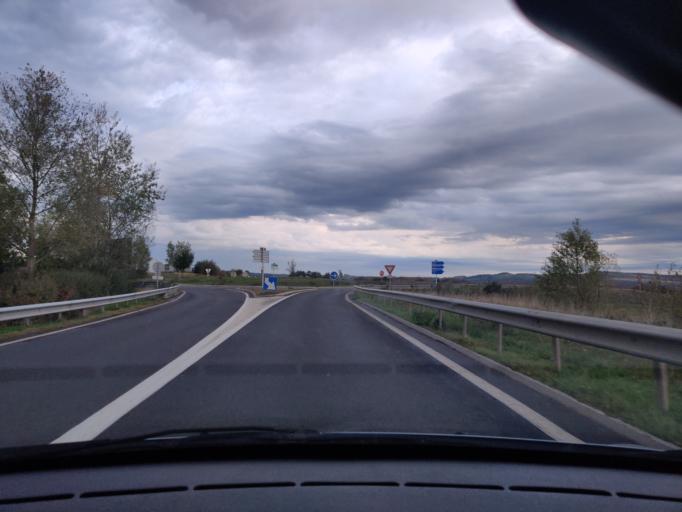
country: FR
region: Auvergne
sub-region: Departement du Puy-de-Dome
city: Combronde
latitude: 45.9925
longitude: 3.0892
